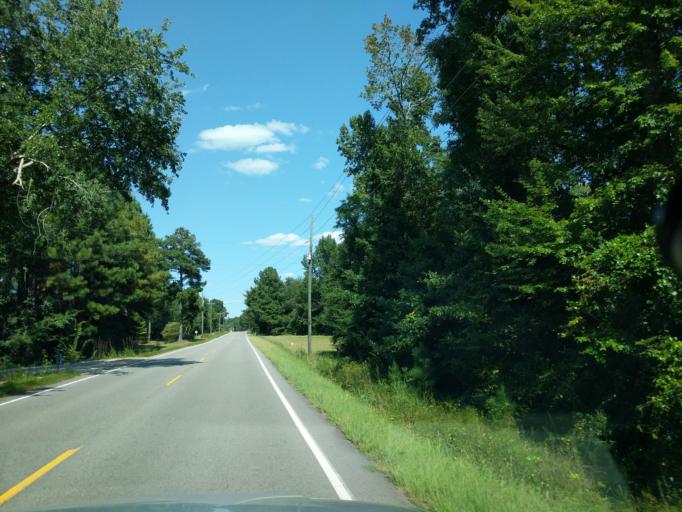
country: US
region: South Carolina
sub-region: Newberry County
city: Prosperity
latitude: 34.1232
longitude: -81.5496
